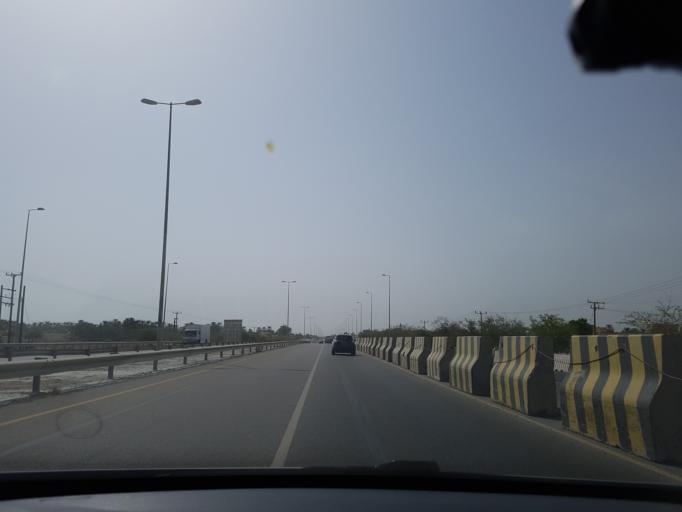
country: OM
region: Al Batinah
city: Al Khaburah
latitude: 23.9959
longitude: 57.0642
